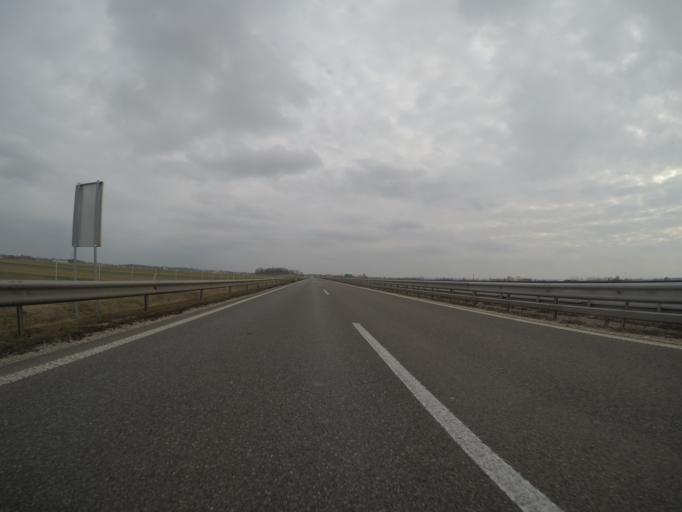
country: SI
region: Turnisce
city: Turnisce
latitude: 46.6240
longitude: 16.2951
